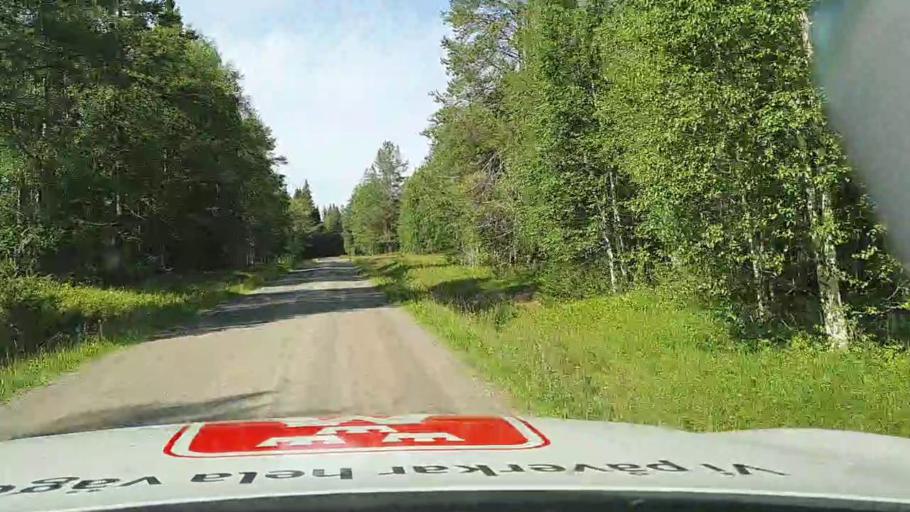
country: SE
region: Jaemtland
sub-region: Stroemsunds Kommun
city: Stroemsund
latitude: 63.7297
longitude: 15.2514
